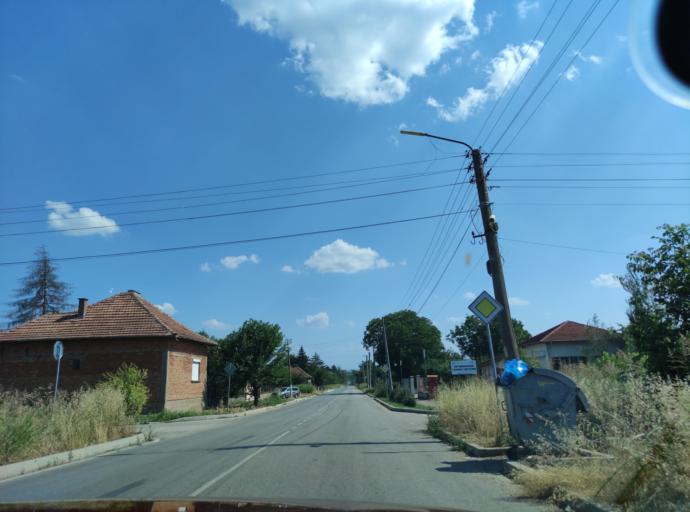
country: BG
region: Pleven
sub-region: Obshtina Cherven Bryag
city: Koynare
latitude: 43.3348
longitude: 24.0664
